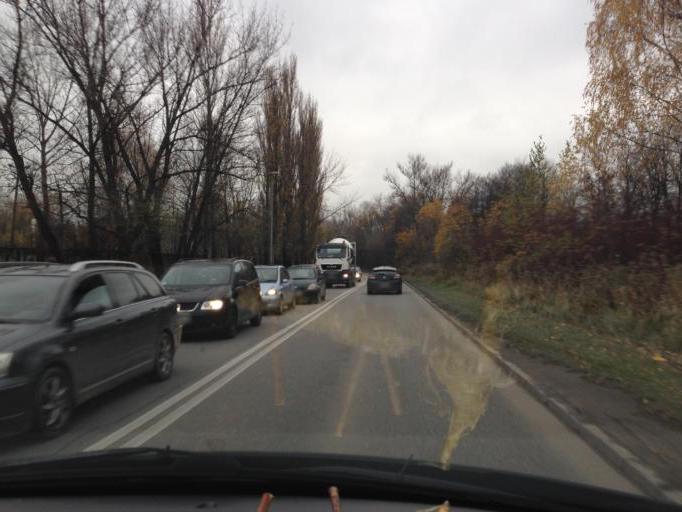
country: PL
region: Lesser Poland Voivodeship
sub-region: Powiat wielicki
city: Kokotow
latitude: 50.0753
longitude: 20.0627
